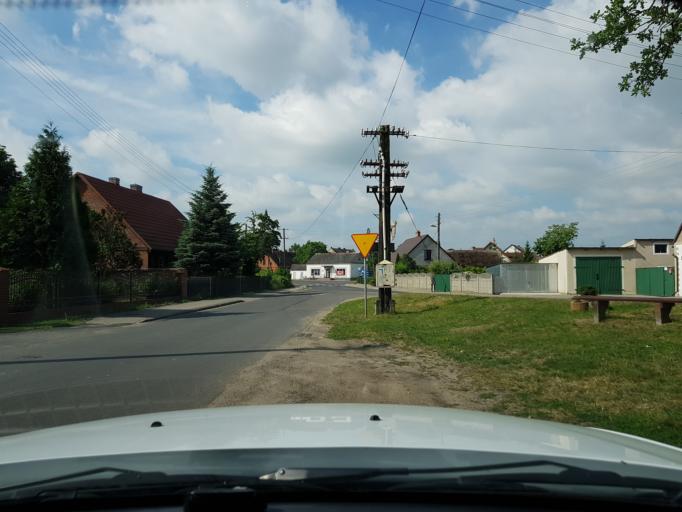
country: PL
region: West Pomeranian Voivodeship
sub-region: Powiat gryfinski
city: Banie
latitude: 53.1305
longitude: 14.6134
